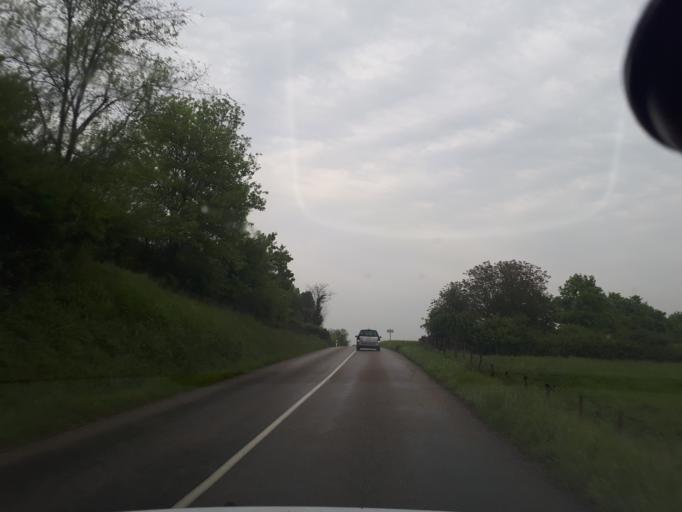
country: FR
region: Rhone-Alpes
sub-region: Departement de l'Isere
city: Frontonas
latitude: 45.6503
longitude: 5.2190
